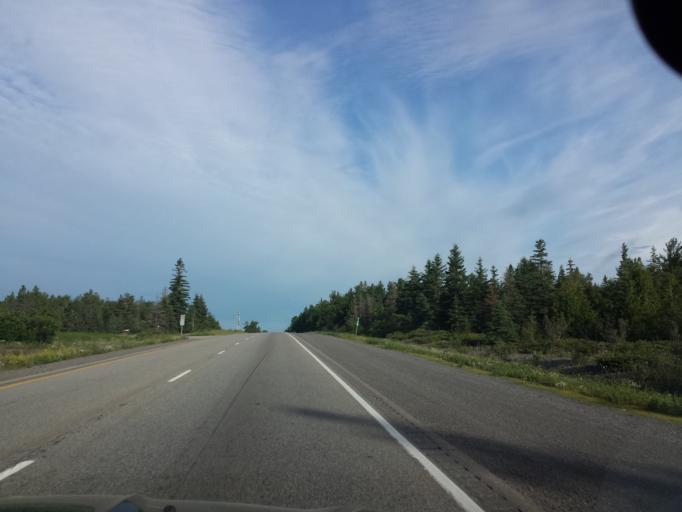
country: CA
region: Ontario
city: Carleton Place
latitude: 45.3269
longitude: -76.1296
